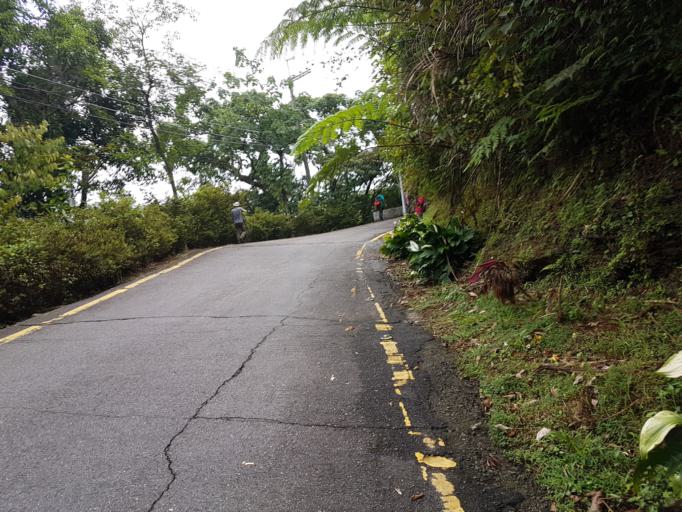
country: TW
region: Taiwan
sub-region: Keelung
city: Keelung
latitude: 25.0514
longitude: 121.6658
